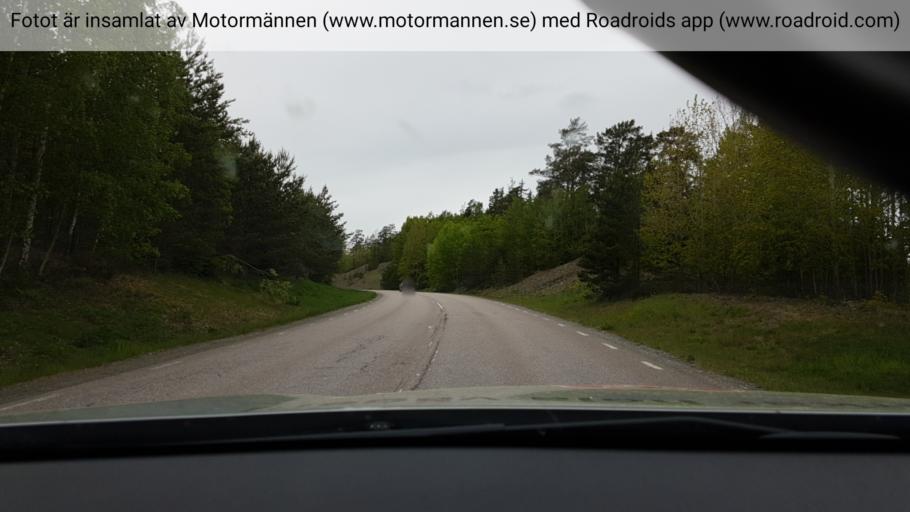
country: SE
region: Stockholm
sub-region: Vaxholms Kommun
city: Vaxholm
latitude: 59.3950
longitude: 18.4047
